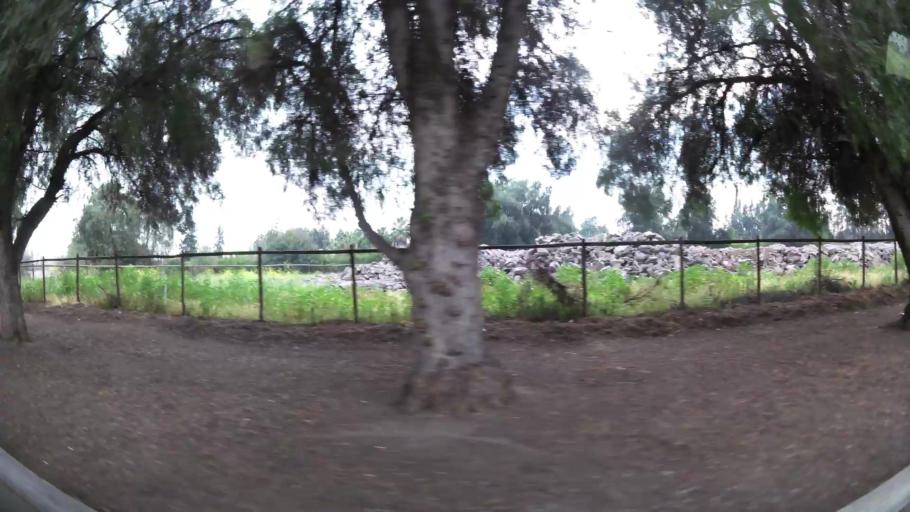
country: CL
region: Santiago Metropolitan
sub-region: Provincia de Chacabuco
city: Chicureo Abajo
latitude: -33.2775
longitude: -70.7051
